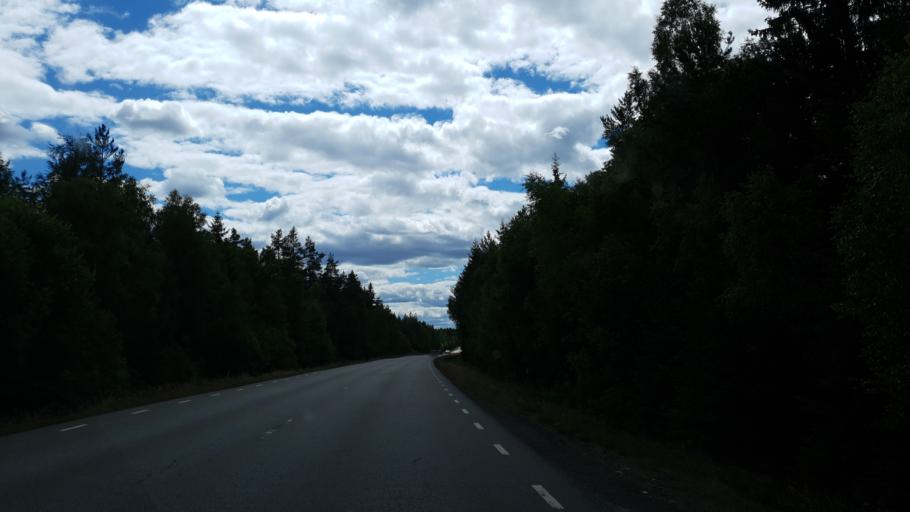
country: SE
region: Kronoberg
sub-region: Uppvidinge Kommun
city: Lenhovda
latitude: 56.9347
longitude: 15.5808
